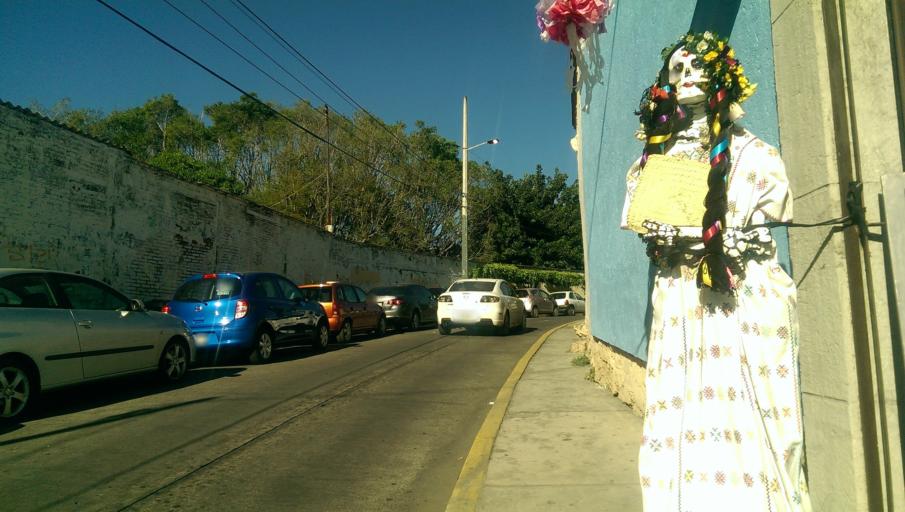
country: MX
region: Morelos
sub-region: Cuernavaca
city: Cuernavaca
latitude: 18.9221
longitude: -99.2379
